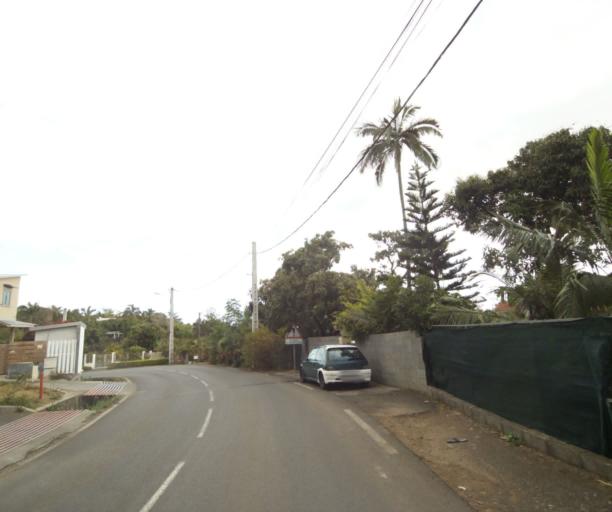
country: RE
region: Reunion
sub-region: Reunion
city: Saint-Paul
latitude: -21.0549
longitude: 55.2832
